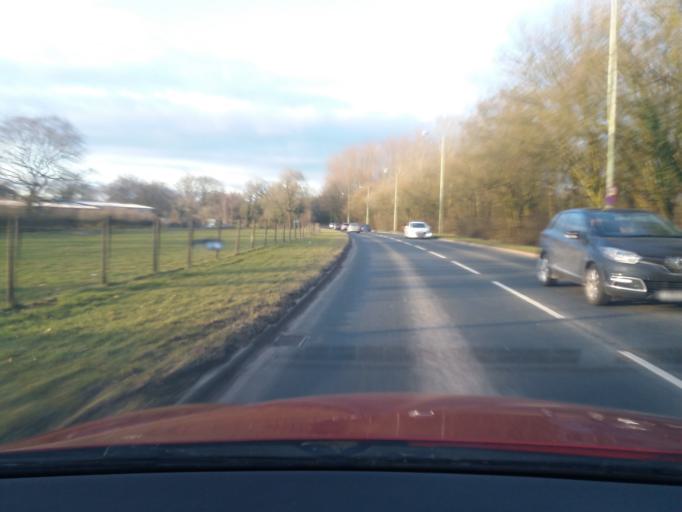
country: GB
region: England
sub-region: Lancashire
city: Euxton
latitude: 53.6641
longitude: -2.6511
